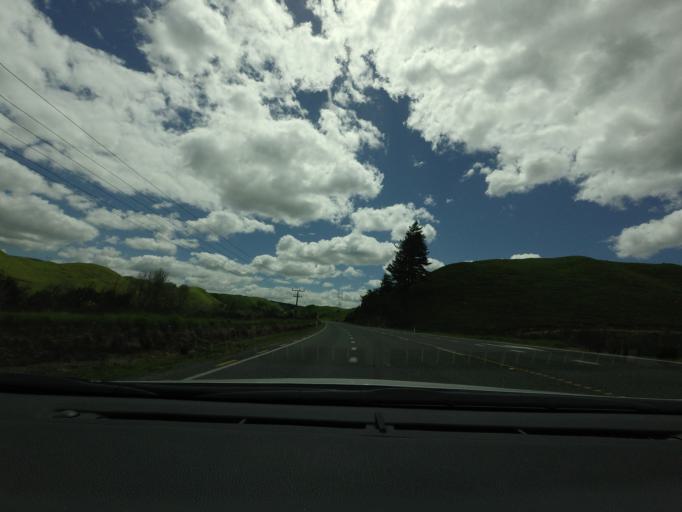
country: NZ
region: Bay of Plenty
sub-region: Rotorua District
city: Rotorua
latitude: -38.3100
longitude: 176.3770
